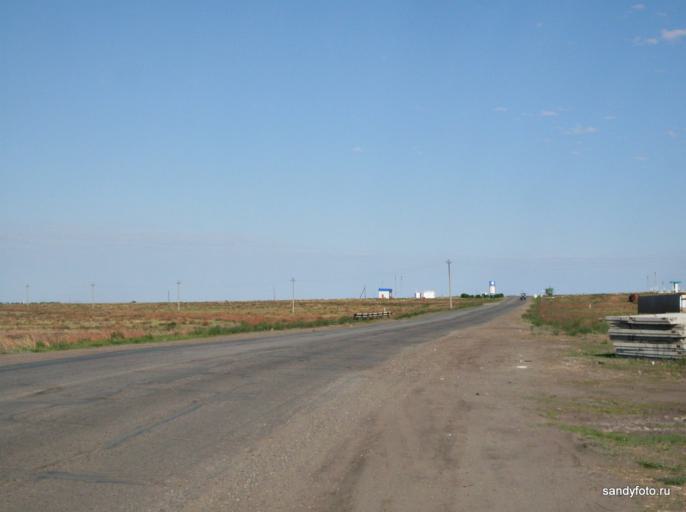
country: RU
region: Chelyabinsk
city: Troitsk
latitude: 54.0982
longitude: 61.5372
